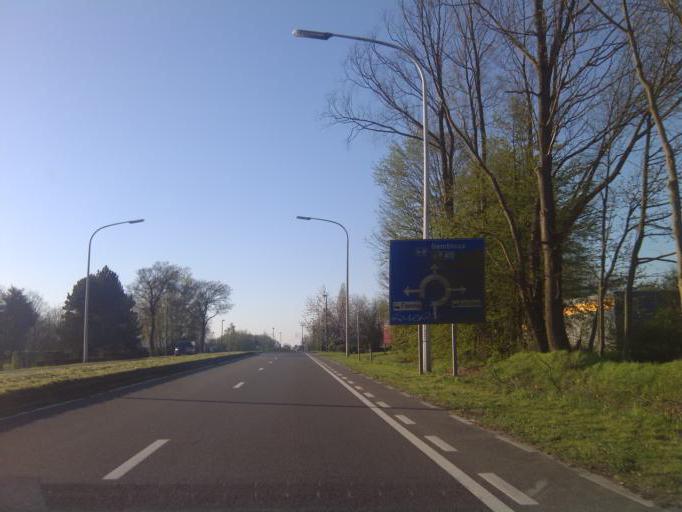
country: BE
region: Wallonia
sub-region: Province du Brabant Wallon
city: Louvain-la-Neuve
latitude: 50.6652
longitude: 4.6301
